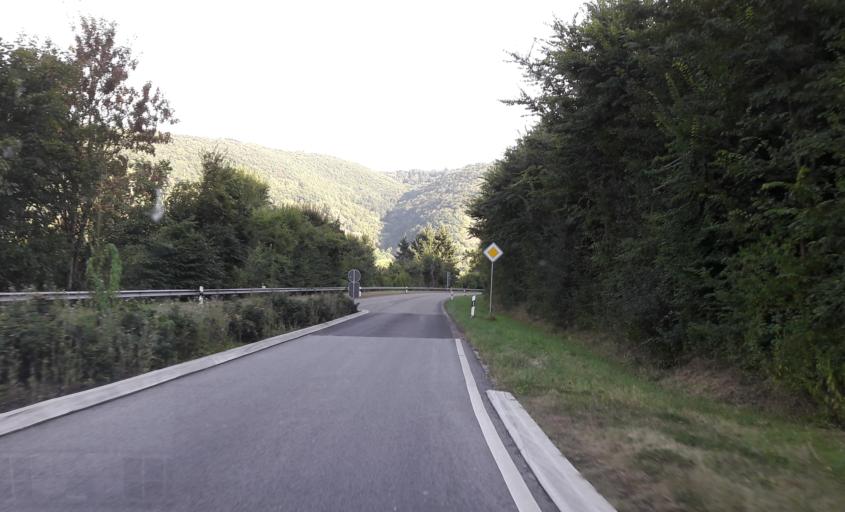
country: DE
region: Rheinland-Pfalz
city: Nehren
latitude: 50.0888
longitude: 7.1993
